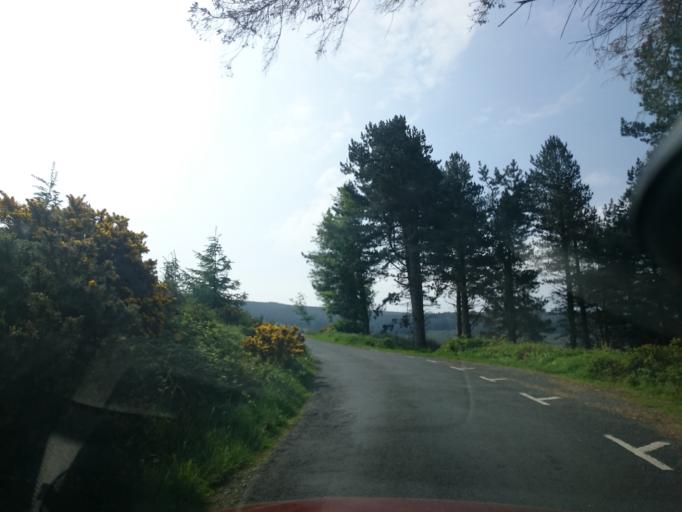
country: IE
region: Leinster
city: Ballinteer
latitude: 53.2545
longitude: -6.2494
